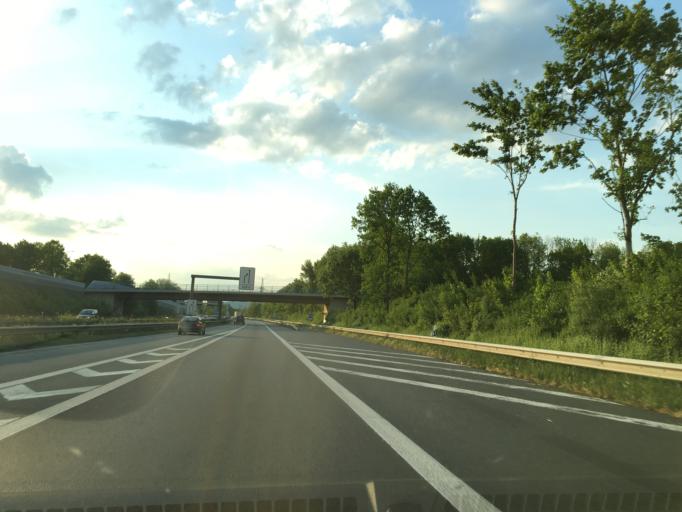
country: DE
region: North Rhine-Westphalia
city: Bad Oeynhausen
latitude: 52.2095
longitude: 8.8378
